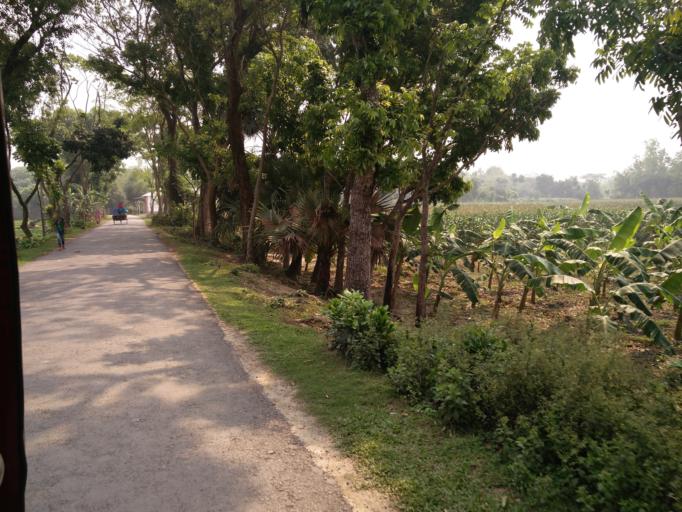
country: BD
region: Dhaka
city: Muktagacha
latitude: 24.9074
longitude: 90.2045
